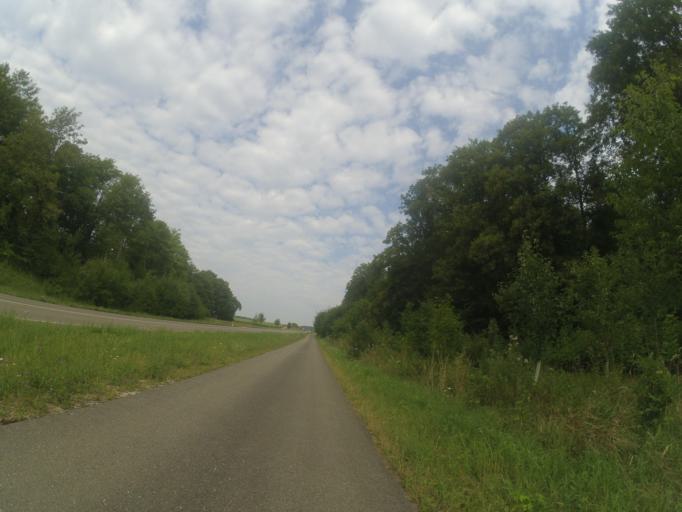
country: DE
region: Baden-Wuerttemberg
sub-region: Tuebingen Region
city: Lonsee
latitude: 48.5111
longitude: 9.9165
